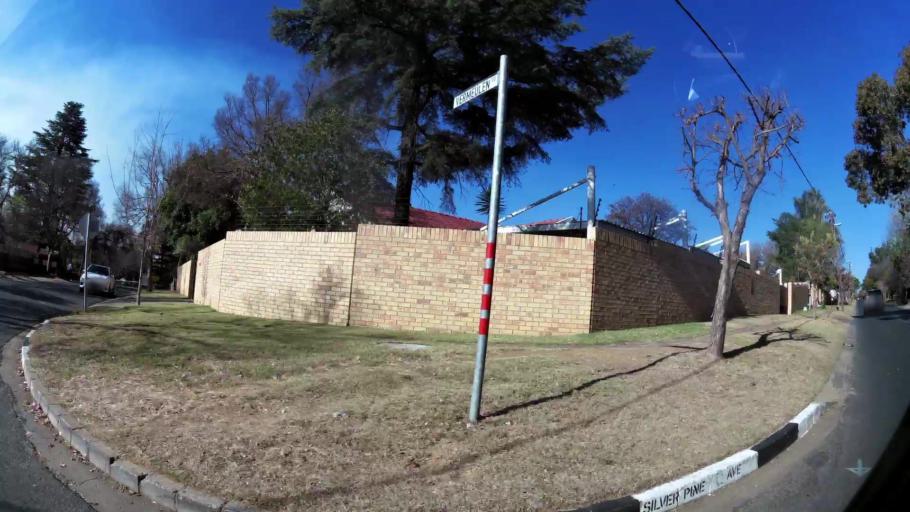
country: ZA
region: Gauteng
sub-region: City of Johannesburg Metropolitan Municipality
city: Roodepoort
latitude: -26.0972
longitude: 27.9775
